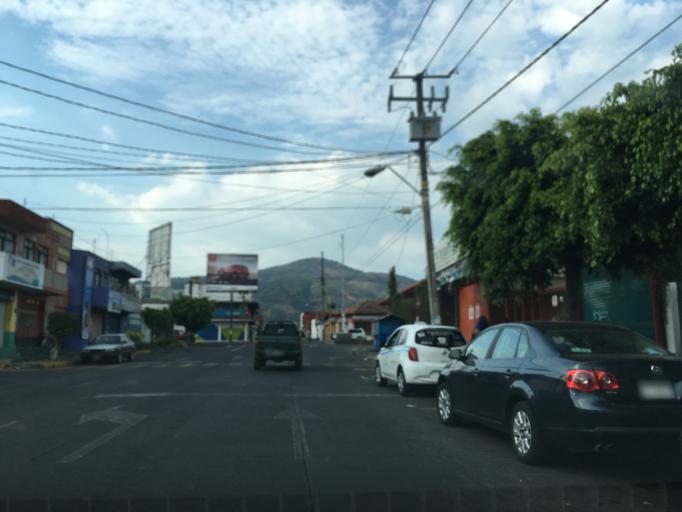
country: MX
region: Michoacan
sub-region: Uruapan
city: Uruapan
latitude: 19.4138
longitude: -102.0571
